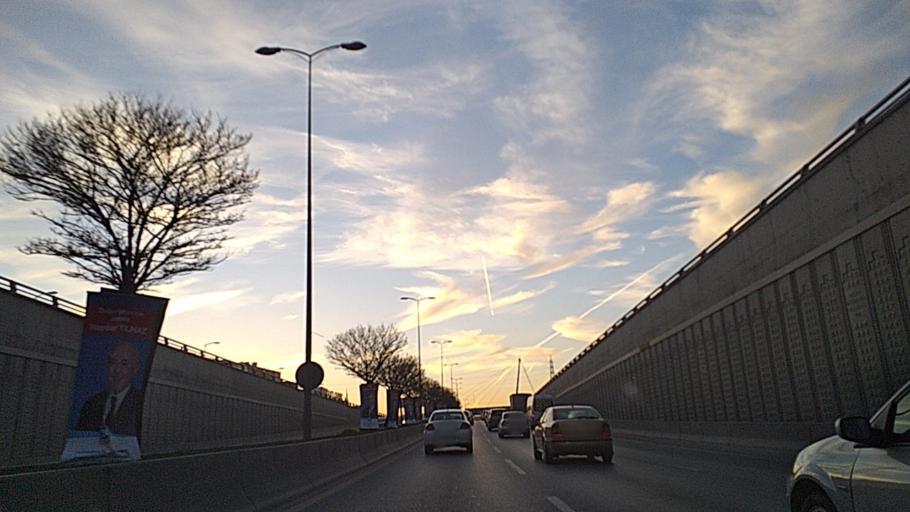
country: TR
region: Ankara
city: Etimesgut
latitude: 39.9658
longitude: 32.6353
